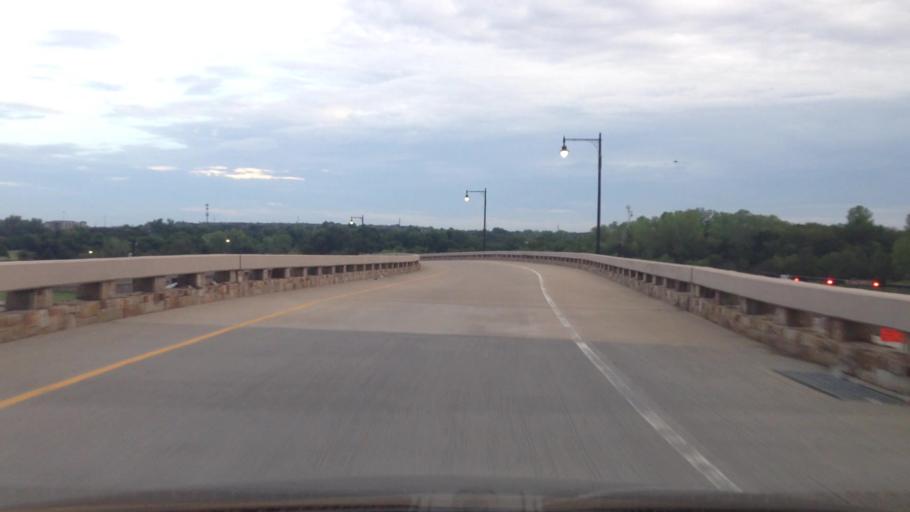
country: US
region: Texas
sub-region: Dallas County
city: Coppell
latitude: 32.9870
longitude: -97.0436
